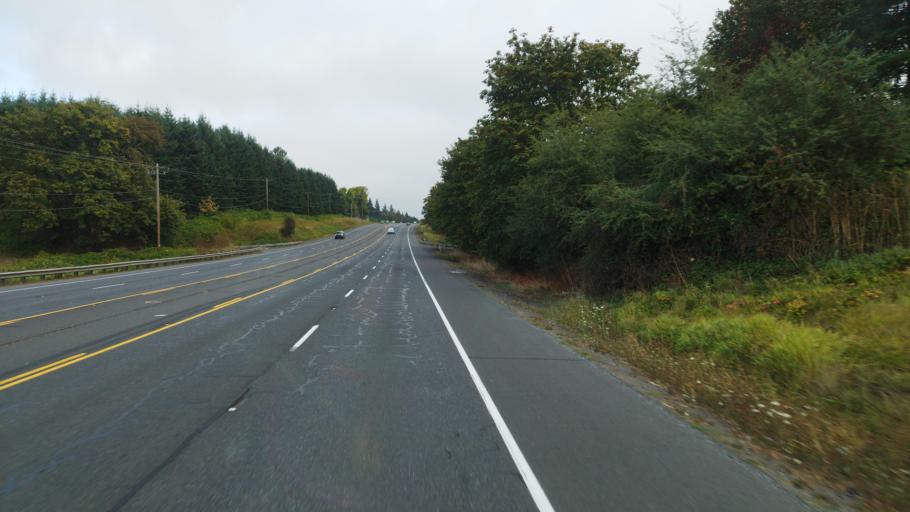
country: US
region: Oregon
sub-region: Columbia County
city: Scappoose
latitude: 45.7881
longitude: -122.8711
